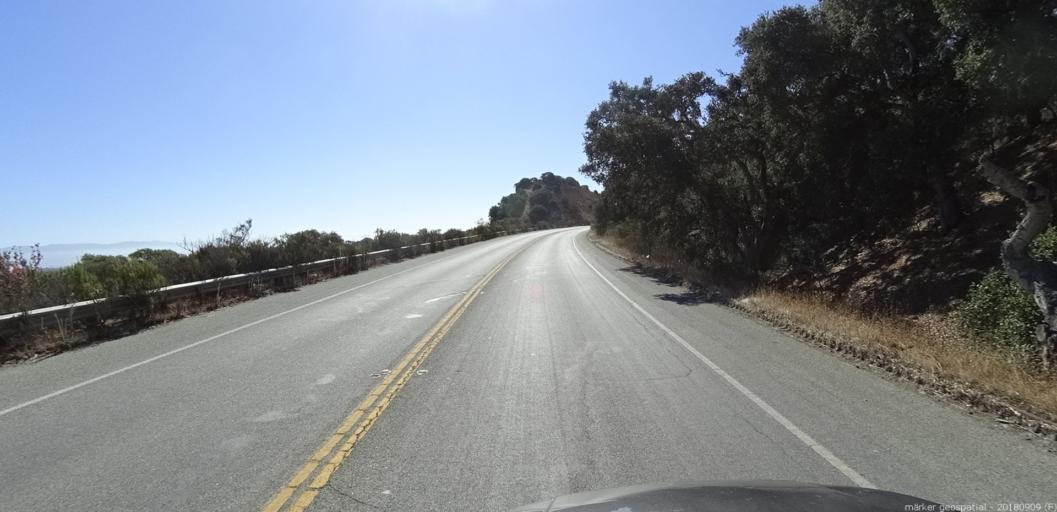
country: US
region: California
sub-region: Monterey County
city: Salinas
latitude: 36.6316
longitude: -121.6934
